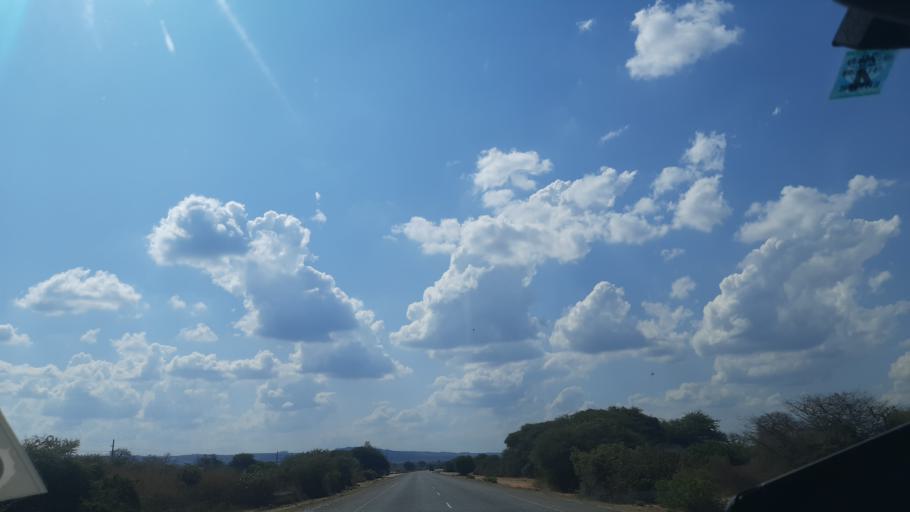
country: TZ
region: Singida
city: Kilimatinde
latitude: -5.8349
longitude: 35.0642
